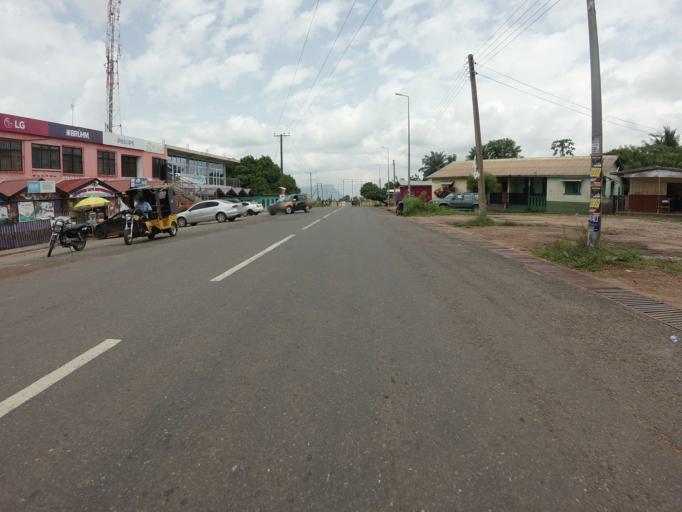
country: GH
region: Volta
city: Ho
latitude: 6.6043
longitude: 0.4660
